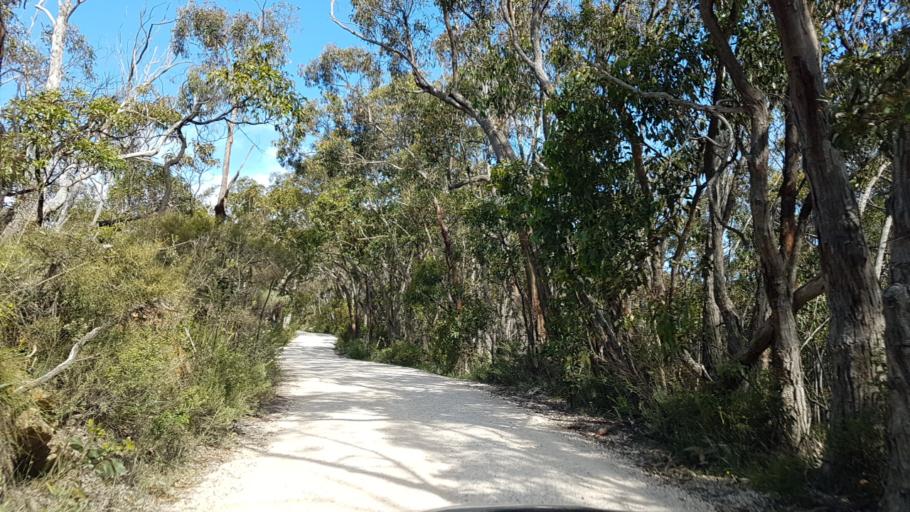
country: AU
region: South Australia
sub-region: Adelaide Hills
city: Adelaide Hills
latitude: -34.9118
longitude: 138.7527
